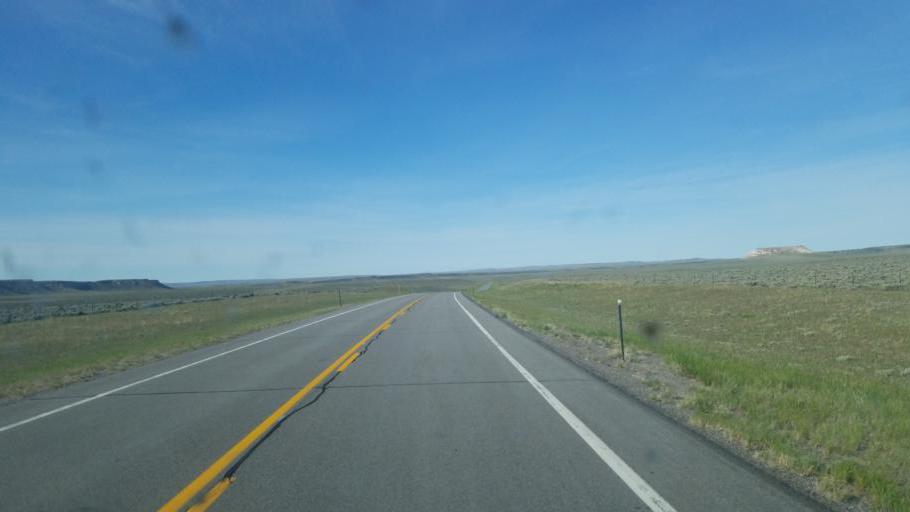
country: US
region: Wyoming
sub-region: Fremont County
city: Riverton
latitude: 42.6619
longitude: -108.1847
